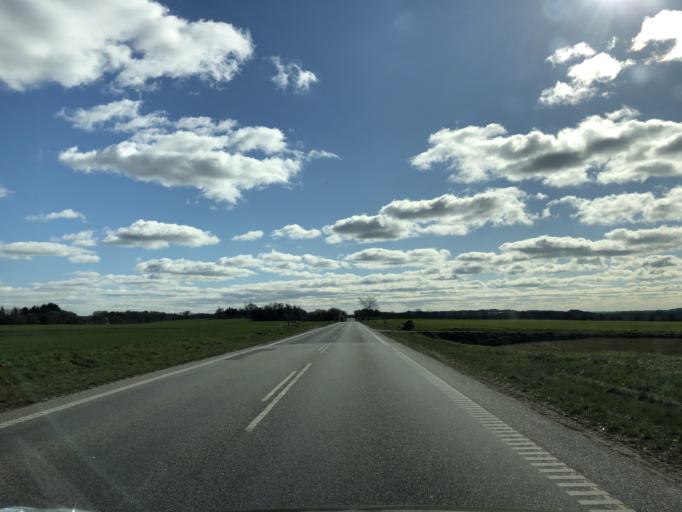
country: DK
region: North Denmark
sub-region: Vesthimmerland Kommune
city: Alestrup
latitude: 56.6147
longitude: 9.6262
